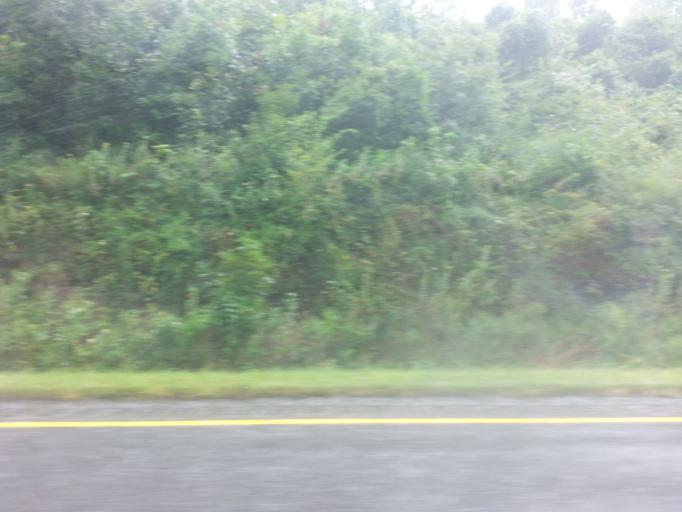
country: US
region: Tennessee
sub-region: Smith County
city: Gordonsville
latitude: 36.1694
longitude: -85.9043
